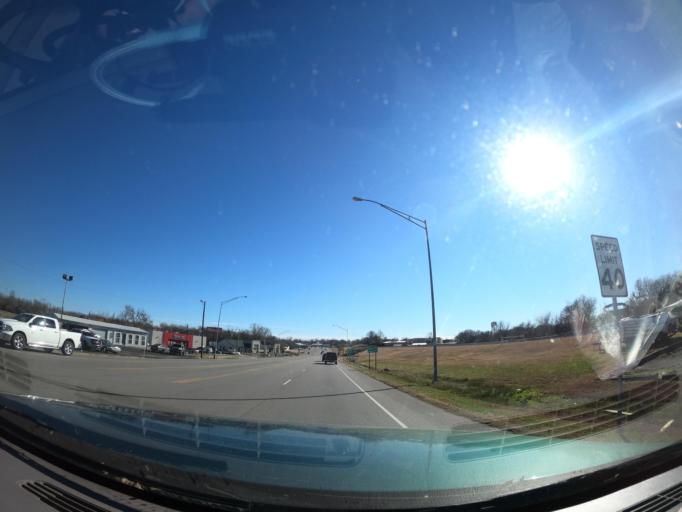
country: US
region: Oklahoma
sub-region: Wagoner County
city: Coweta
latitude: 35.9579
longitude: -95.6510
